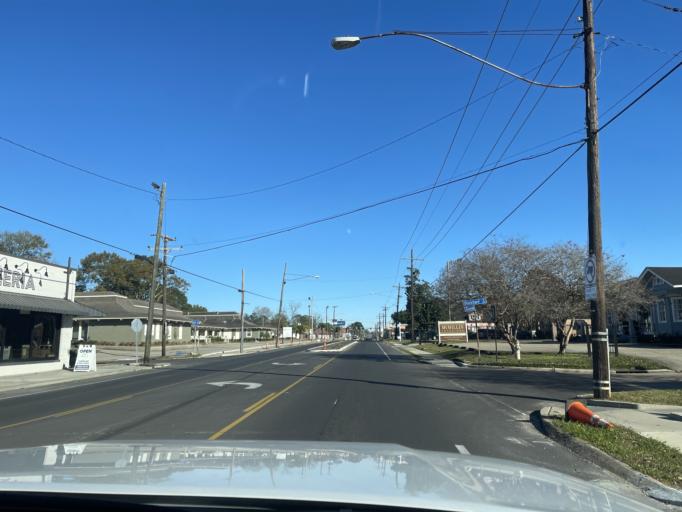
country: US
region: Louisiana
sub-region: East Baton Rouge Parish
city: Baton Rouge
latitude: 30.4443
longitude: -91.1500
